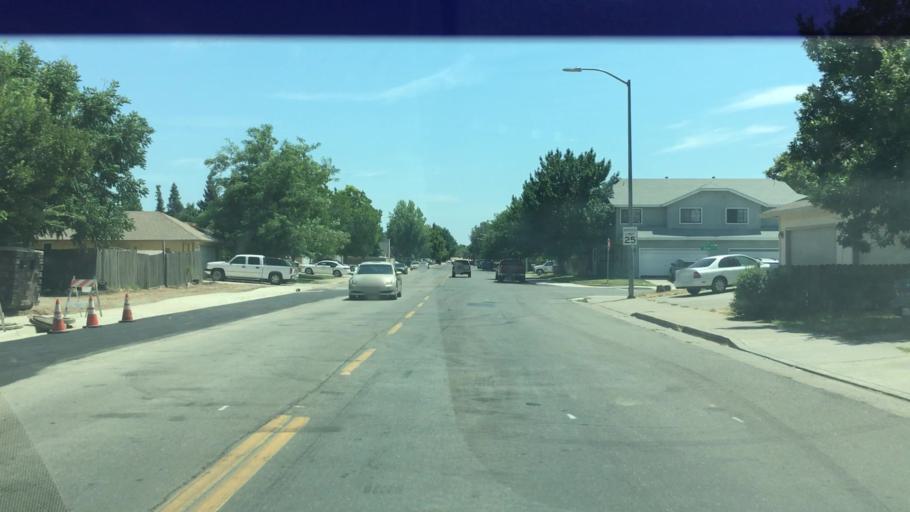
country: US
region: California
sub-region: Sacramento County
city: Galt
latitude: 38.2470
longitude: -121.3094
